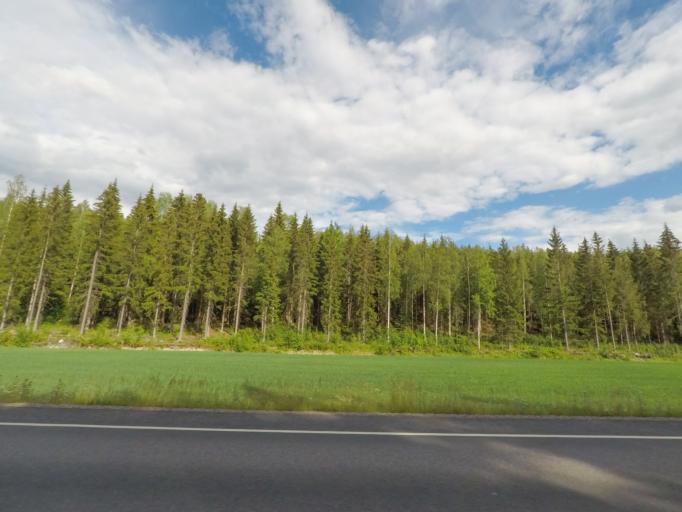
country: FI
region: Uusimaa
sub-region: Porvoo
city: Pukkila
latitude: 60.7911
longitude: 25.4655
